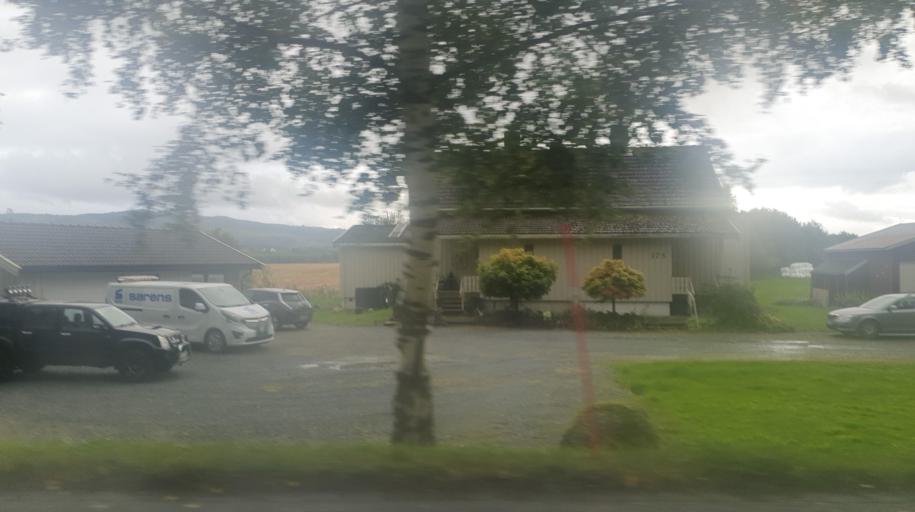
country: NO
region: Nord-Trondelag
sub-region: Verdal
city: Verdal
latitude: 63.7961
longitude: 11.5290
